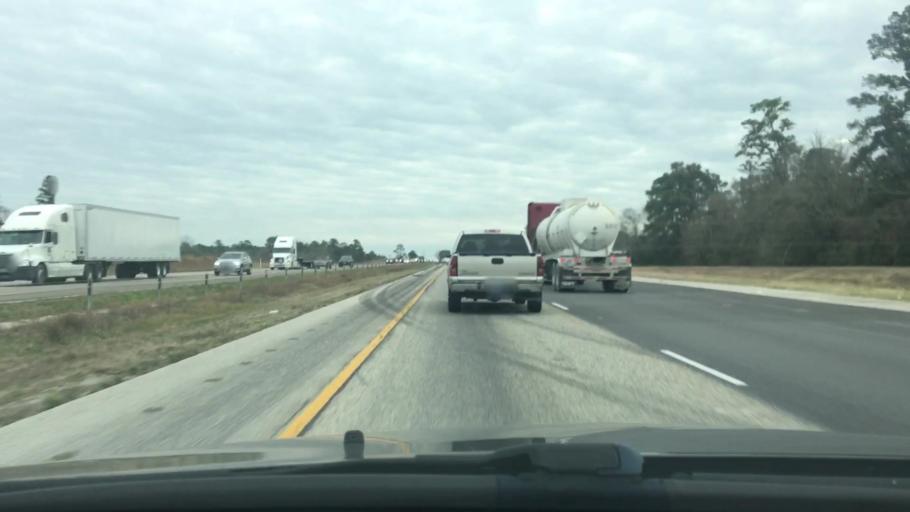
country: US
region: Texas
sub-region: Walker County
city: Huntsville
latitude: 30.7789
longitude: -95.6539
